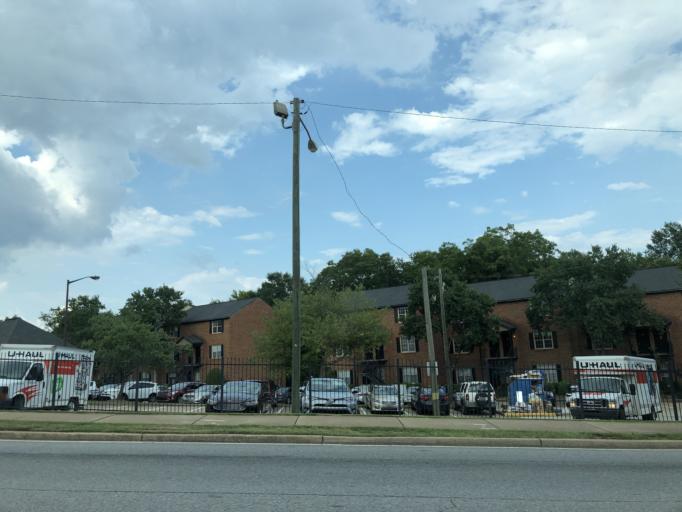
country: US
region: Georgia
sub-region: Clarke County
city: Athens
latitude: 33.9553
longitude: -83.3688
